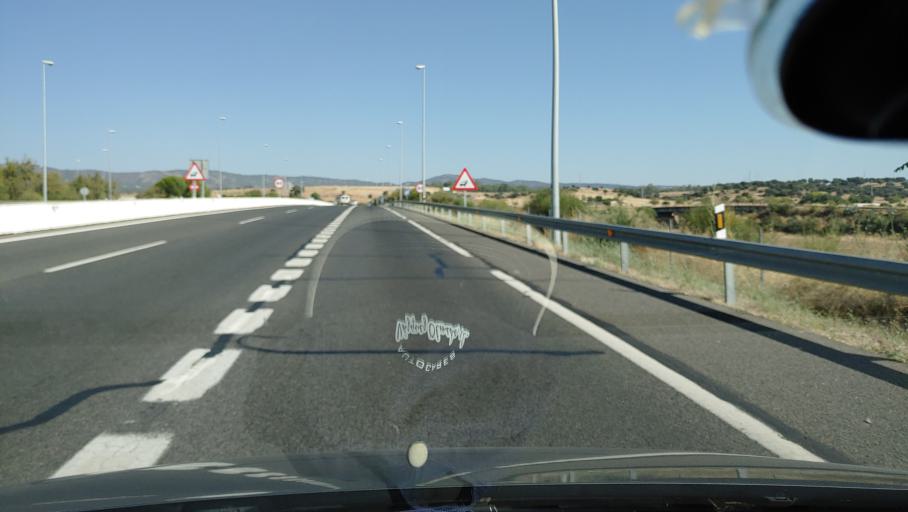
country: ES
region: Andalusia
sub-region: Province of Cordoba
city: Cordoba
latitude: 37.9024
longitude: -4.7500
